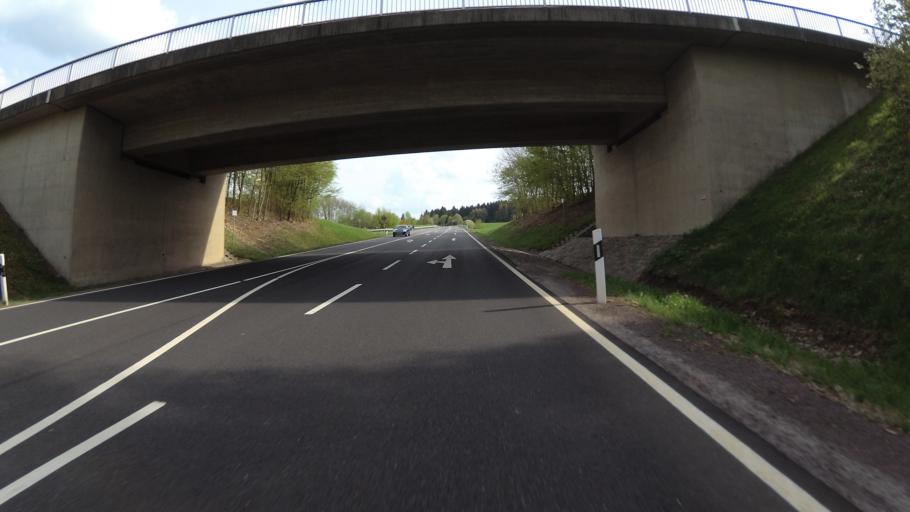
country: DE
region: Rheinland-Pfalz
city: Horschhausen
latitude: 50.2426
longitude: 6.9302
